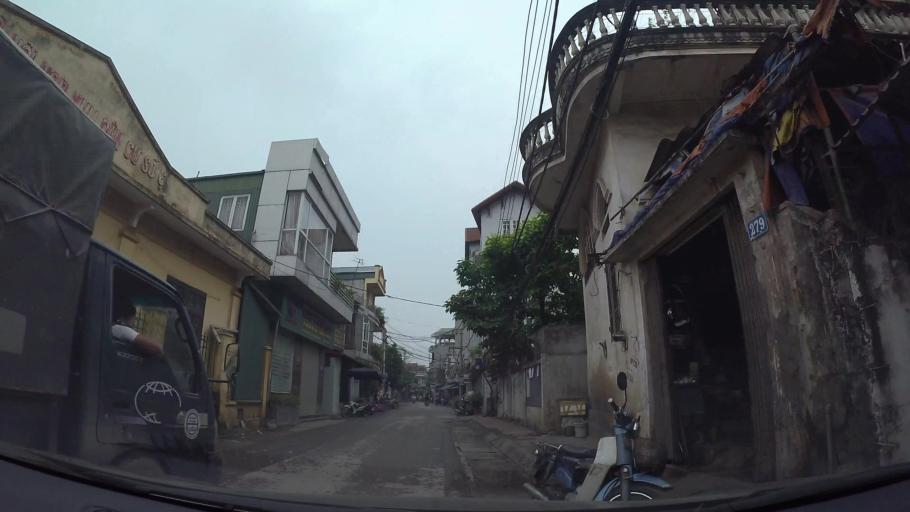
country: VN
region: Ha Noi
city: Van Dien
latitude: 20.9660
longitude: 105.8735
